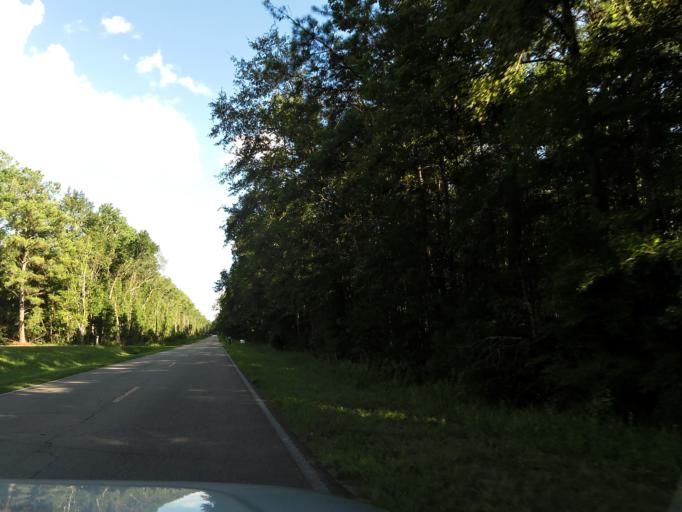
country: US
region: Florida
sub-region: Wakulla County
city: Crawfordville
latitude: 30.0681
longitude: -84.5052
